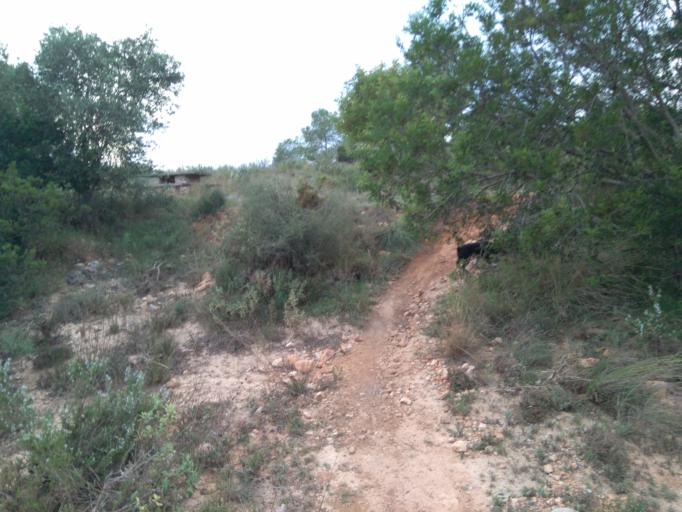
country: ES
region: Valencia
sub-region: Provincia de Valencia
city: Benimodo
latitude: 39.1985
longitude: -0.5846
